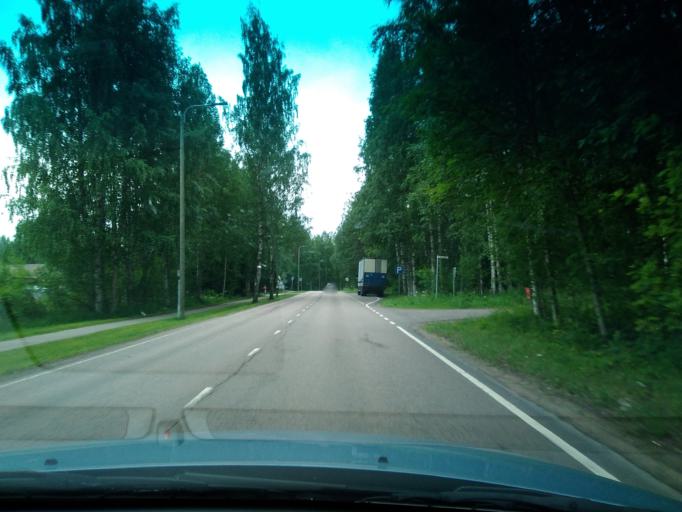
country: FI
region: Central Finland
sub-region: Keuruu
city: Multia
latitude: 62.4036
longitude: 24.7929
